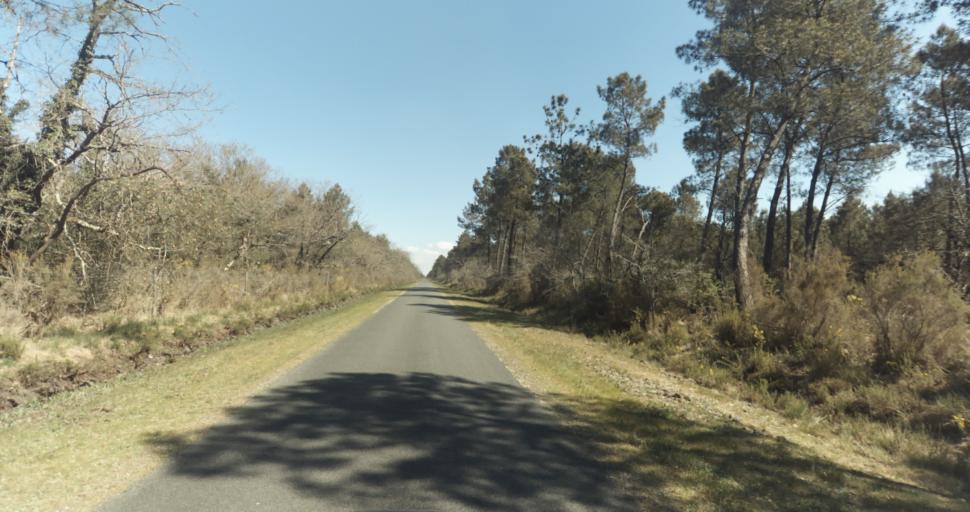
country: FR
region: Aquitaine
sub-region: Departement de la Gironde
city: Martignas-sur-Jalle
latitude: 44.7750
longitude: -0.8055
